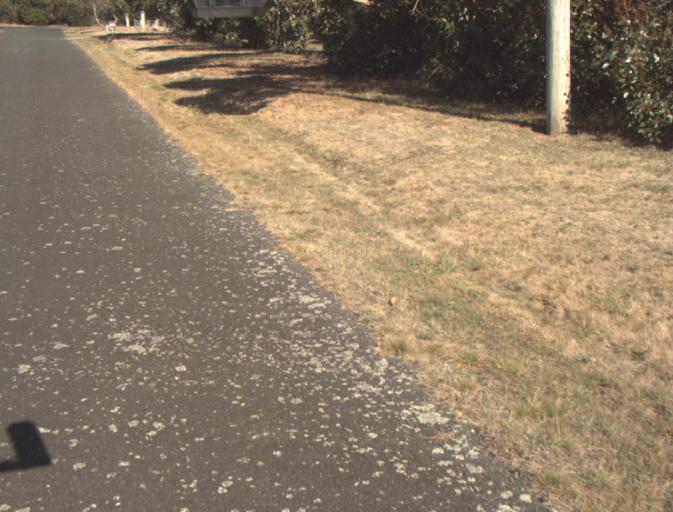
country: AU
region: Tasmania
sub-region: Launceston
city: Mayfield
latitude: -41.3277
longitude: 147.0579
